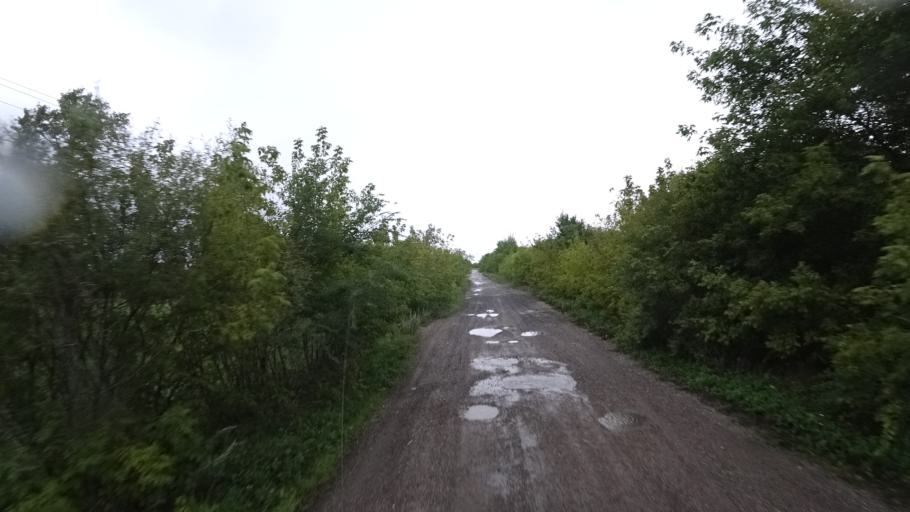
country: RU
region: Primorskiy
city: Chernigovka
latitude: 44.4025
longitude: 132.5316
